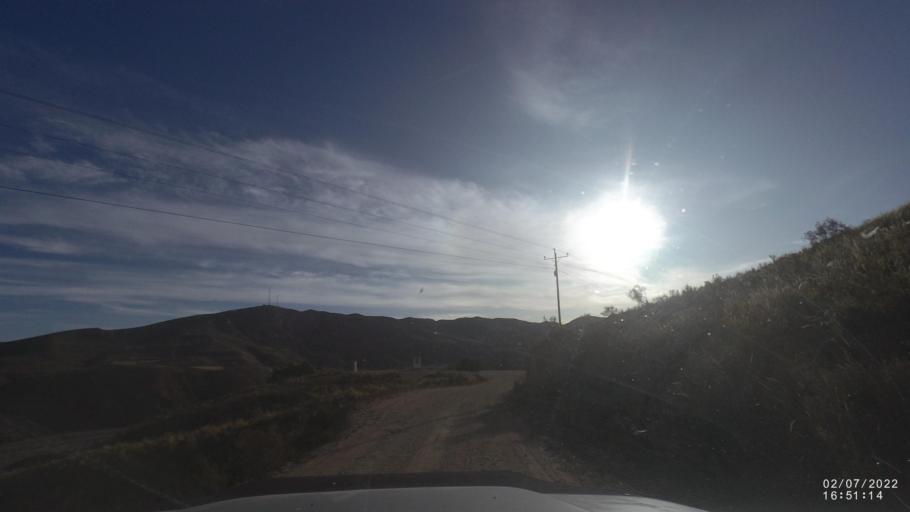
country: BO
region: Cochabamba
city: Irpa Irpa
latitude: -17.9708
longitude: -66.5334
